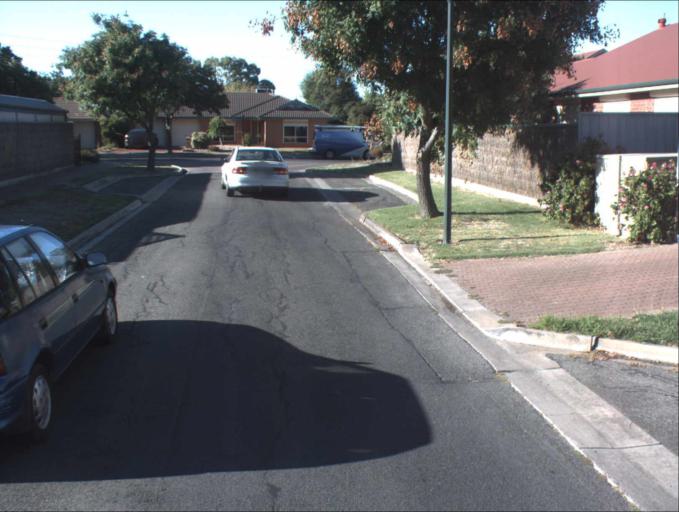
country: AU
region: South Australia
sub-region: Port Adelaide Enfield
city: Gilles Plains
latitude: -34.8575
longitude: 138.6440
